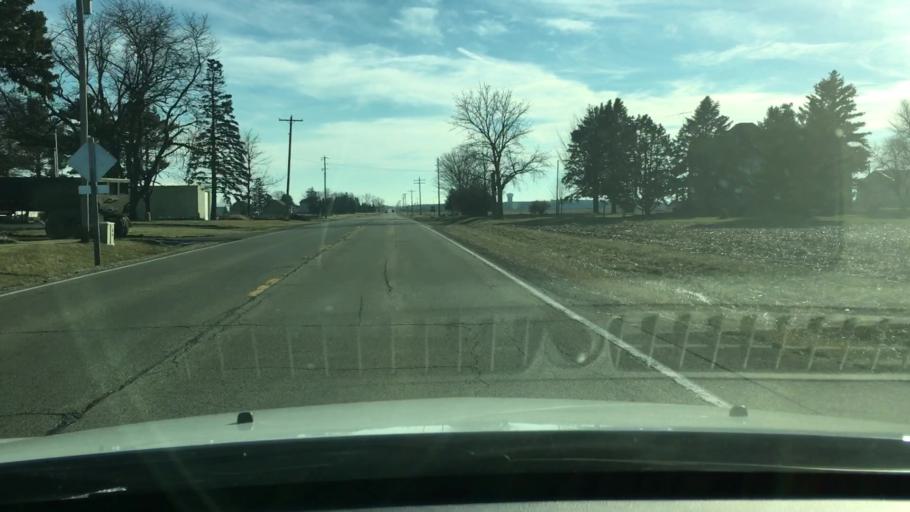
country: US
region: Illinois
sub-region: LaSalle County
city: Peru
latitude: 41.3950
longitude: -89.1257
